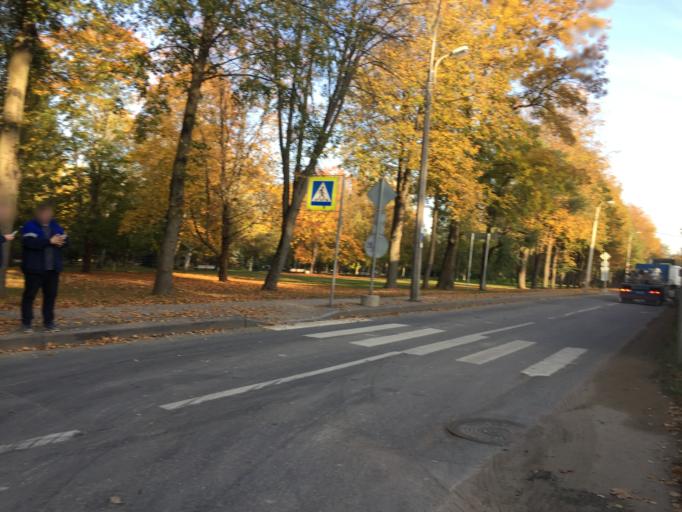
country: RU
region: St.-Petersburg
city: Pushkin
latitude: 59.7264
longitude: 30.3940
